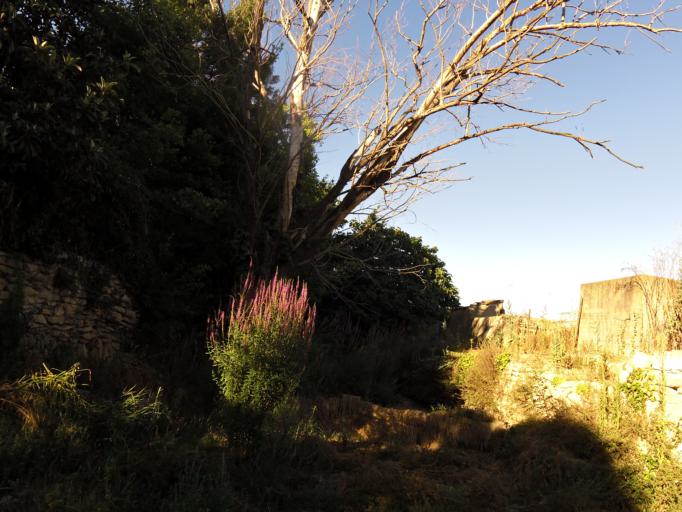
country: FR
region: Languedoc-Roussillon
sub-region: Departement du Gard
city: Villevieille
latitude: 43.7888
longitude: 4.1237
